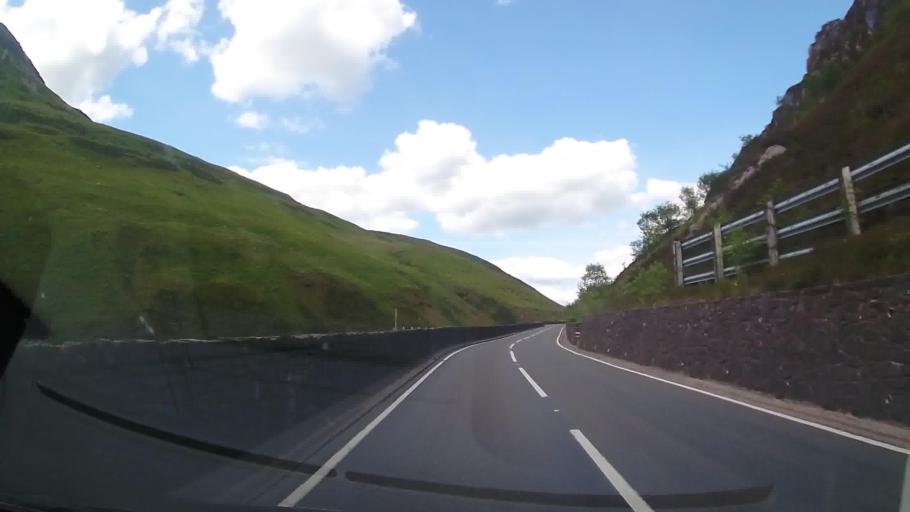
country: GB
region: Wales
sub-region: Gwynedd
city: Corris
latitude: 52.7008
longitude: -3.8536
